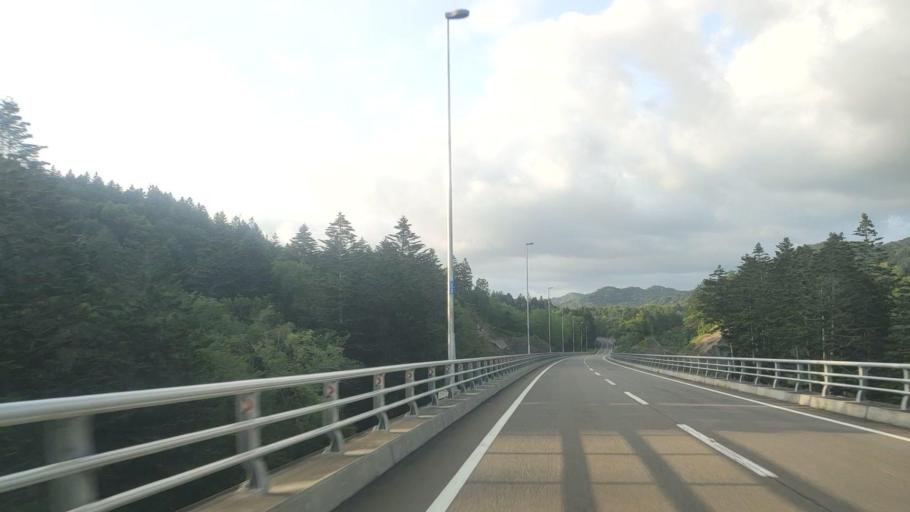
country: JP
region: Hokkaido
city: Bibai
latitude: 43.1080
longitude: 142.0982
